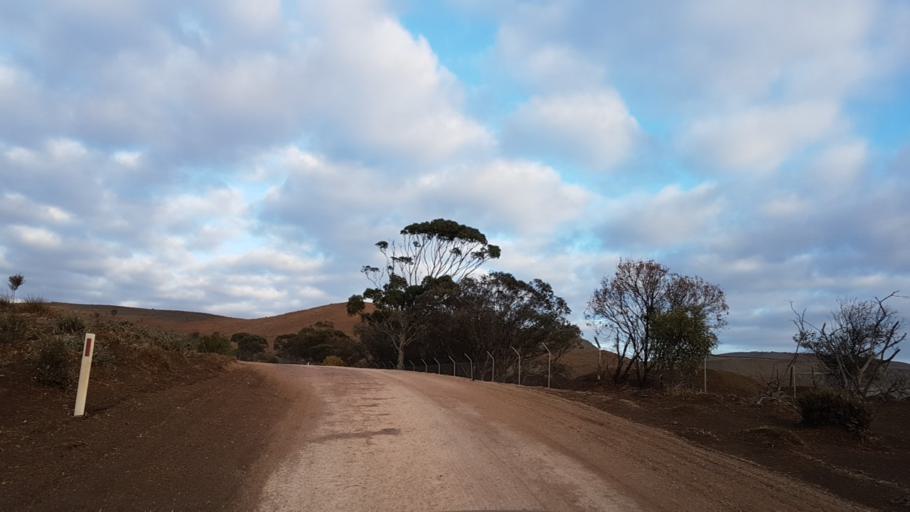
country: AU
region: South Australia
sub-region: Mount Barker
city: Callington
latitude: -35.0967
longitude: 139.0104
